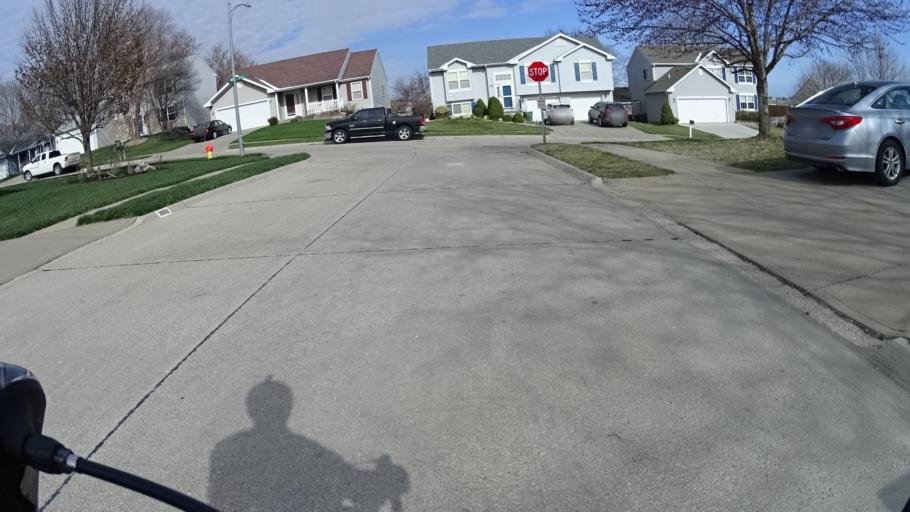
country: US
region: Nebraska
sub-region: Sarpy County
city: Offutt Air Force Base
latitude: 41.1106
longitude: -95.9577
